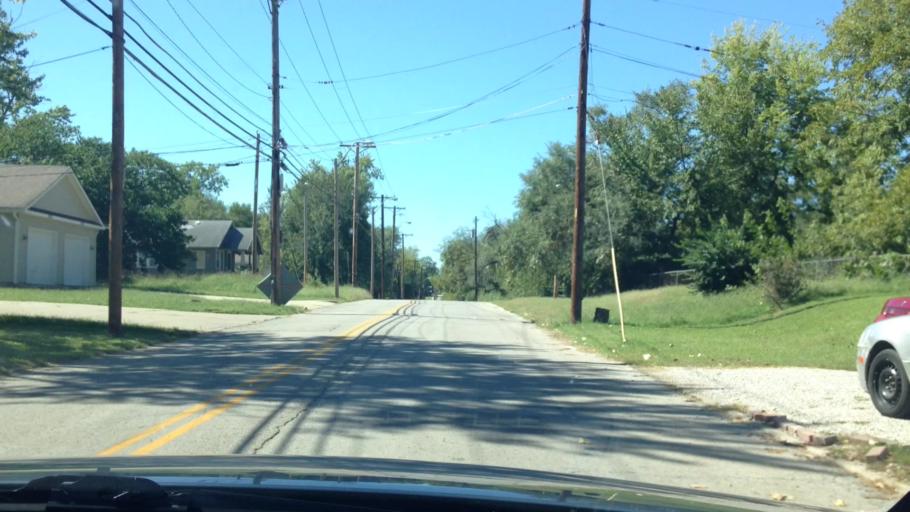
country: US
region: Missouri
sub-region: Jackson County
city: Raytown
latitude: 39.0185
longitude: -94.5308
